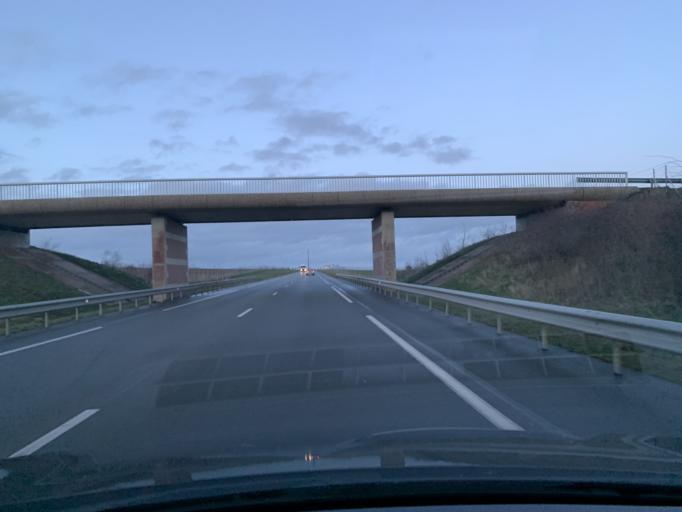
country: FR
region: Nord-Pas-de-Calais
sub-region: Departement du Nord
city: Escaudoeuvres
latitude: 50.1554
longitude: 3.2948
